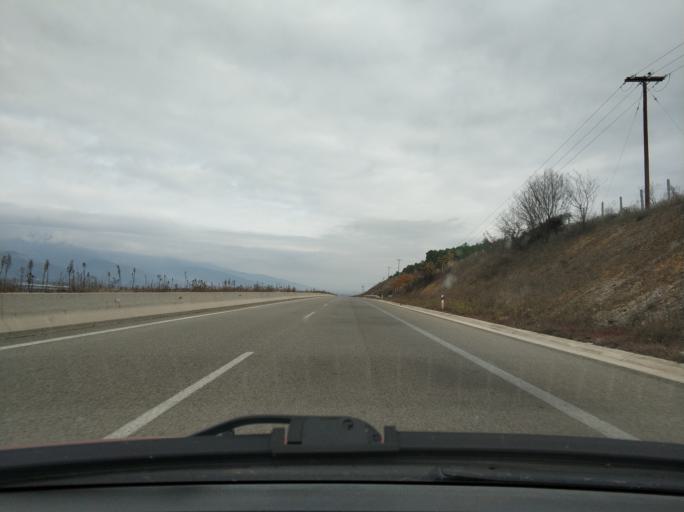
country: GR
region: Central Macedonia
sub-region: Nomos Serron
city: Rodolivos
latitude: 40.8080
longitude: 24.0343
